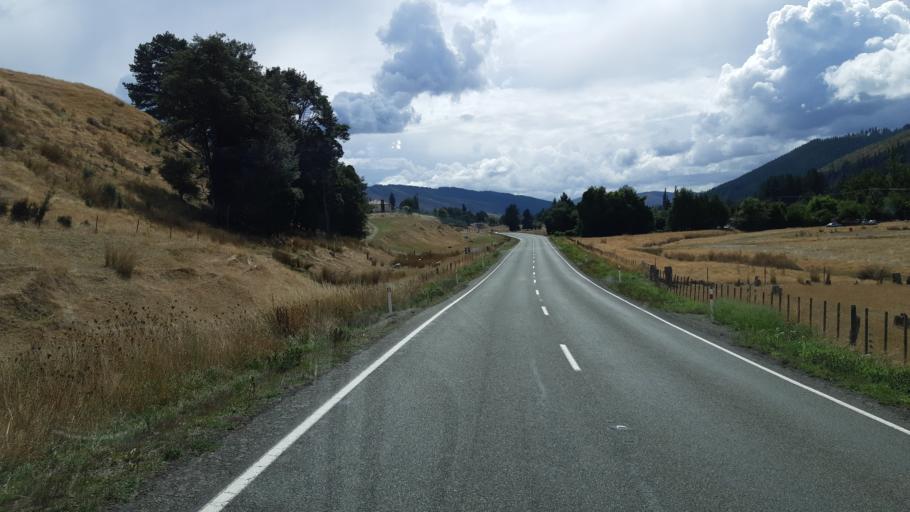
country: NZ
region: Tasman
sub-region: Tasman District
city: Wakefield
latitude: -41.4897
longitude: 172.7980
